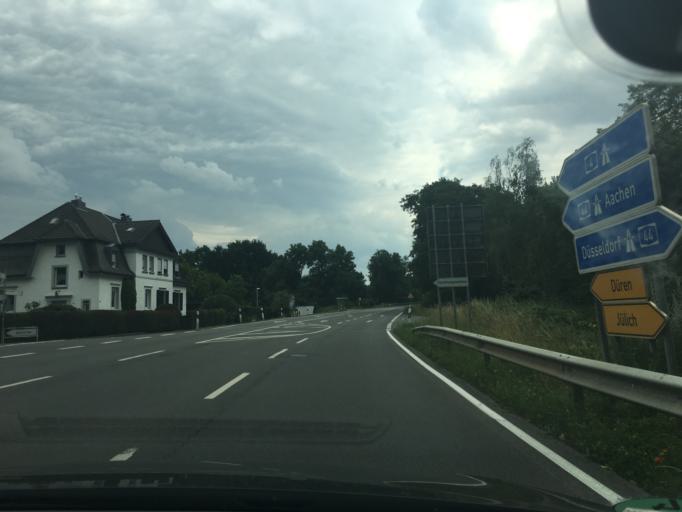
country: DE
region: North Rhine-Westphalia
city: Julich
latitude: 50.9080
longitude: 6.3794
